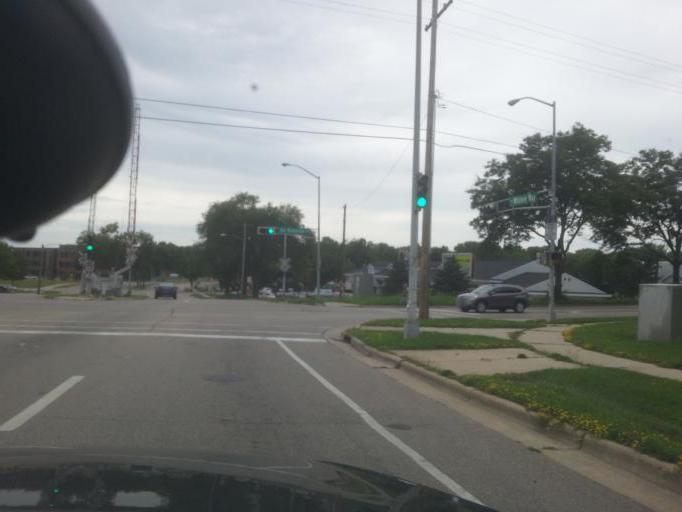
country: US
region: Wisconsin
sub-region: Dane County
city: Shorewood Hills
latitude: 43.0738
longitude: -89.4673
